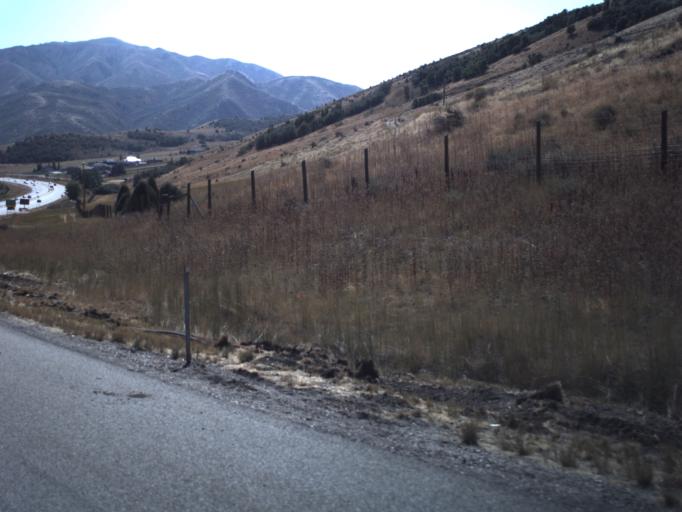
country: US
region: Utah
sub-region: Box Elder County
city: Brigham City
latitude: 41.5170
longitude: -111.9406
